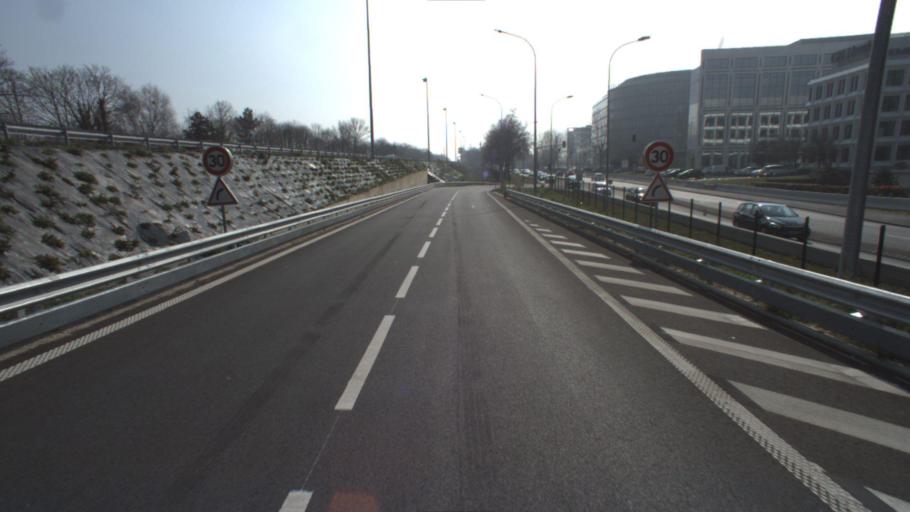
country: FR
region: Ile-de-France
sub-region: Departement du Val-de-Marne
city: Rungis
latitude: 48.7488
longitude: 2.3570
